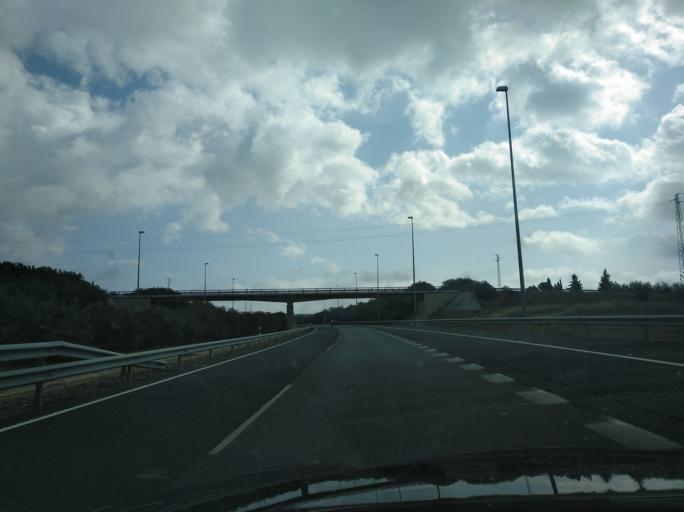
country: ES
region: Andalusia
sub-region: Provincia de Huelva
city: Cartaya
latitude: 37.3312
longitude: -7.1475
